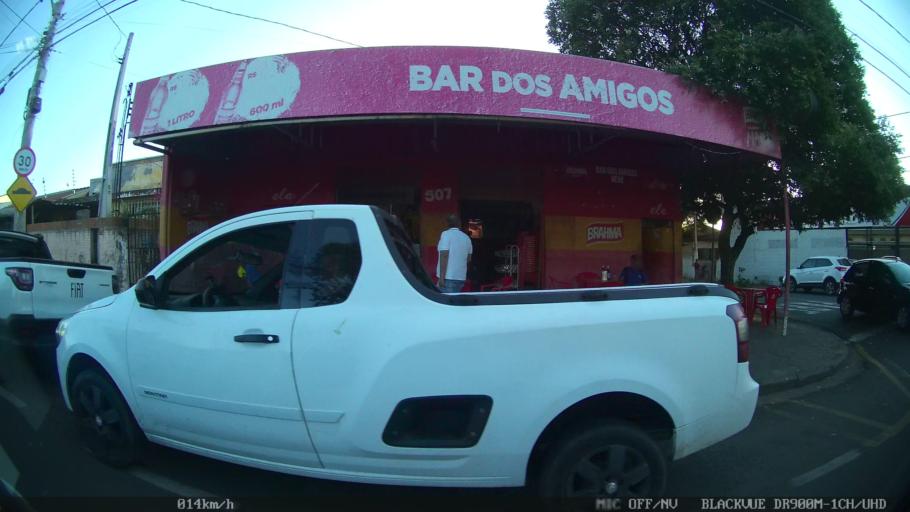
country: BR
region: Sao Paulo
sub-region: Sao Jose Do Rio Preto
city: Sao Jose do Rio Preto
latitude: -20.7932
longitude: -49.3696
